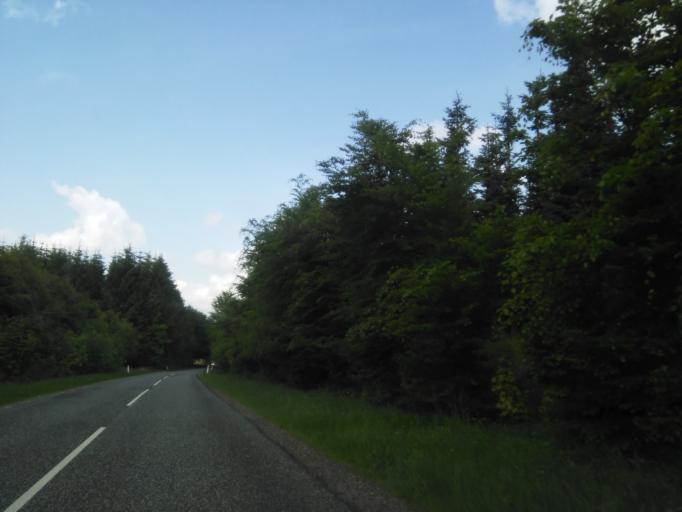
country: DK
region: Central Jutland
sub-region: Favrskov Kommune
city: Hammel
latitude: 56.2560
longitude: 9.9081
